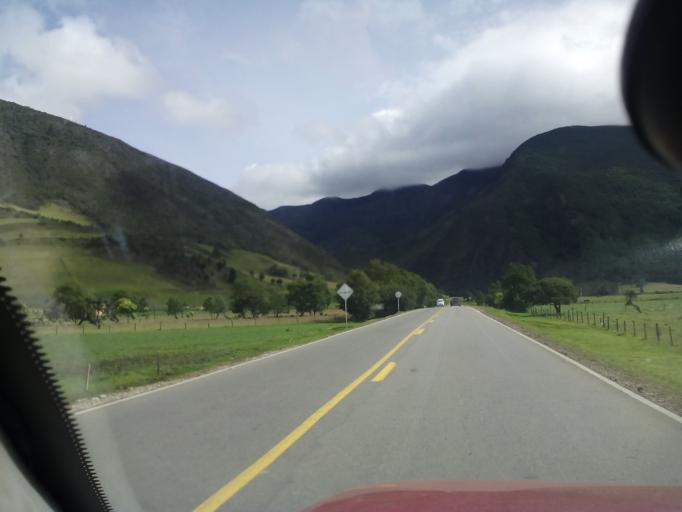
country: CO
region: Boyaca
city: Arcabuco
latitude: 5.7096
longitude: -73.3730
